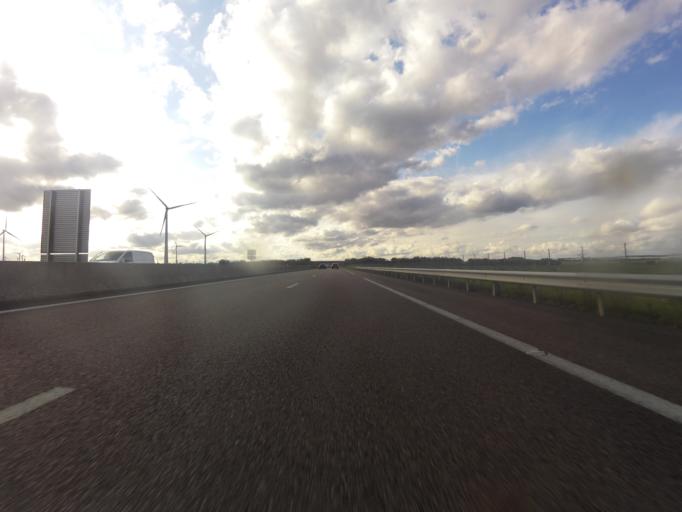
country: FR
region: Picardie
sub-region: Departement de la Somme
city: Poix-de-Picardie
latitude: 49.8131
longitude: 1.9412
